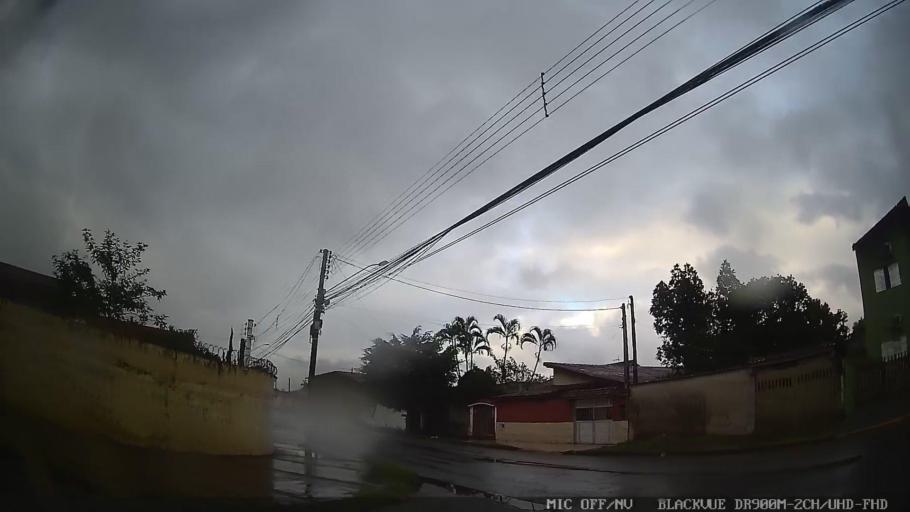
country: BR
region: Sao Paulo
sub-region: Itanhaem
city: Itanhaem
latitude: -24.1696
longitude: -46.7738
